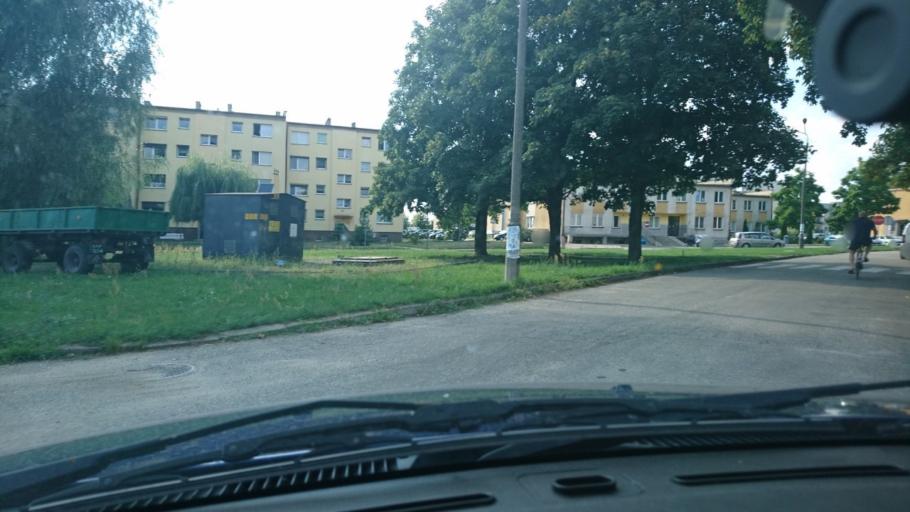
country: PL
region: Greater Poland Voivodeship
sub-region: Powiat ostrowski
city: Odolanow
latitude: 51.5779
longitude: 17.6607
